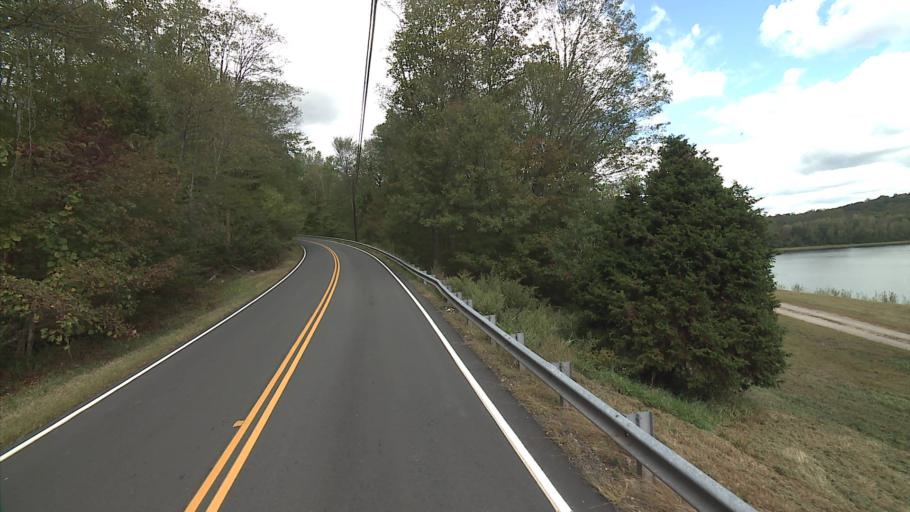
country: US
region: Connecticut
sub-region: Middlesex County
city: Higganum
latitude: 41.4030
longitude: -72.6046
